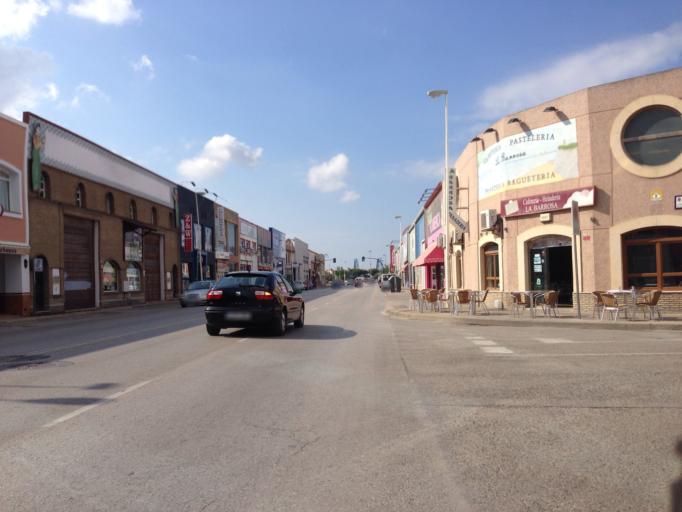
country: ES
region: Andalusia
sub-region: Provincia de Cadiz
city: Chiclana de la Frontera
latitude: 36.4277
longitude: -6.1517
